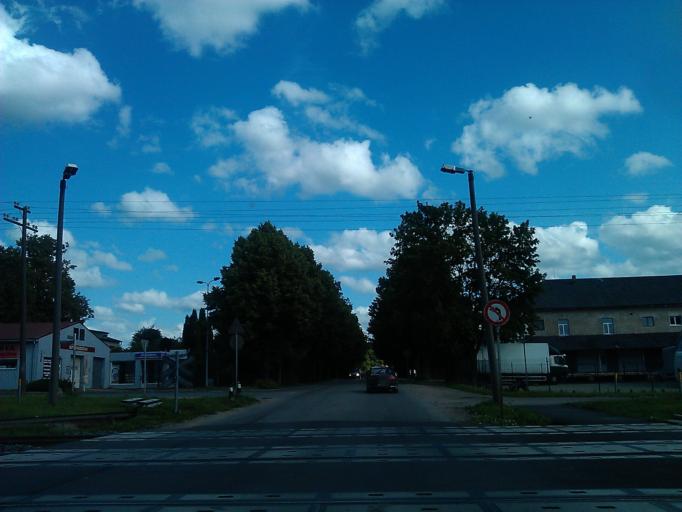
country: LV
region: Cesu Rajons
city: Cesis
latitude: 57.3162
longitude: 25.2855
